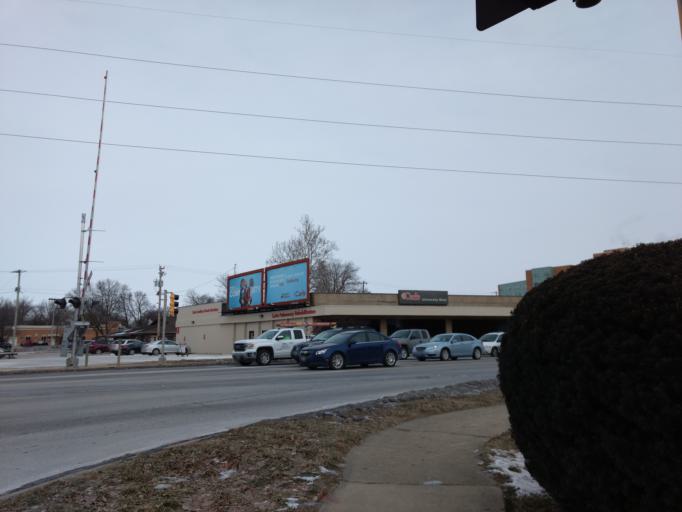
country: US
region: Illinois
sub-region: Champaign County
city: Urbana
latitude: 40.1163
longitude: -88.2192
